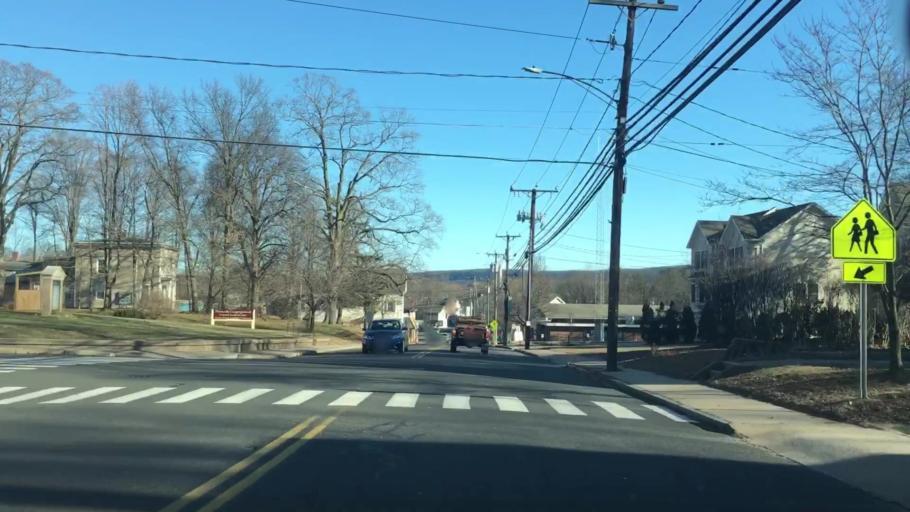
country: US
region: Connecticut
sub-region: New Haven County
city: Cheshire Village
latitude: 41.5879
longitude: -72.8946
